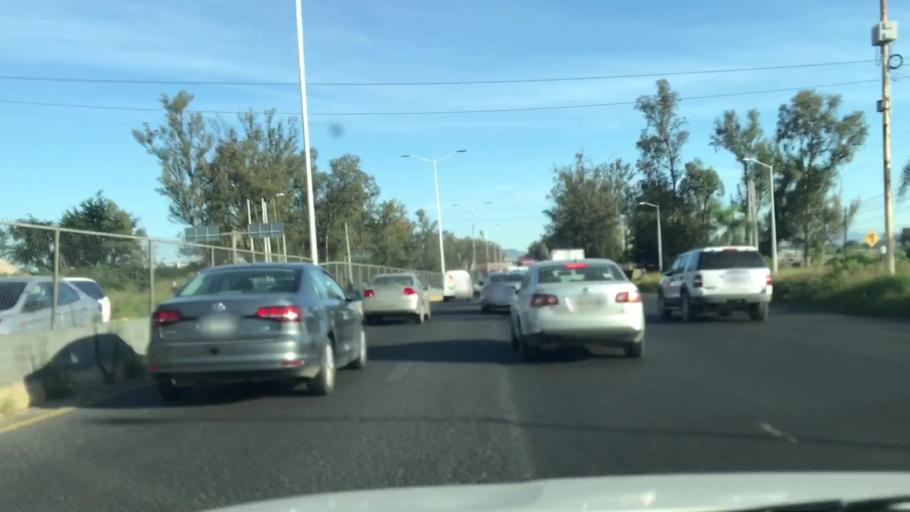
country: MX
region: Jalisco
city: Guadalajara
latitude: 20.6740
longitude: -103.4551
